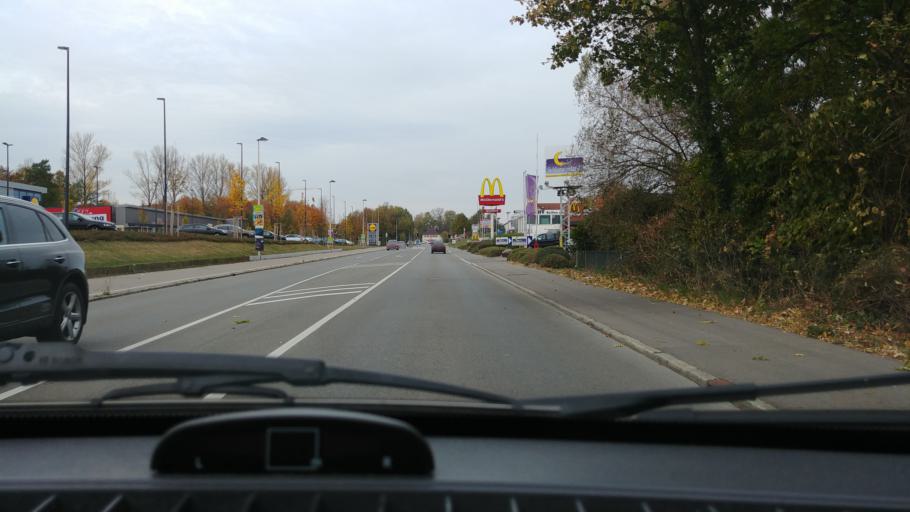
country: DE
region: Baden-Wuerttemberg
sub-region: Regierungsbezirk Stuttgart
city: Crailsheim
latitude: 49.1425
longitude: 10.0495
